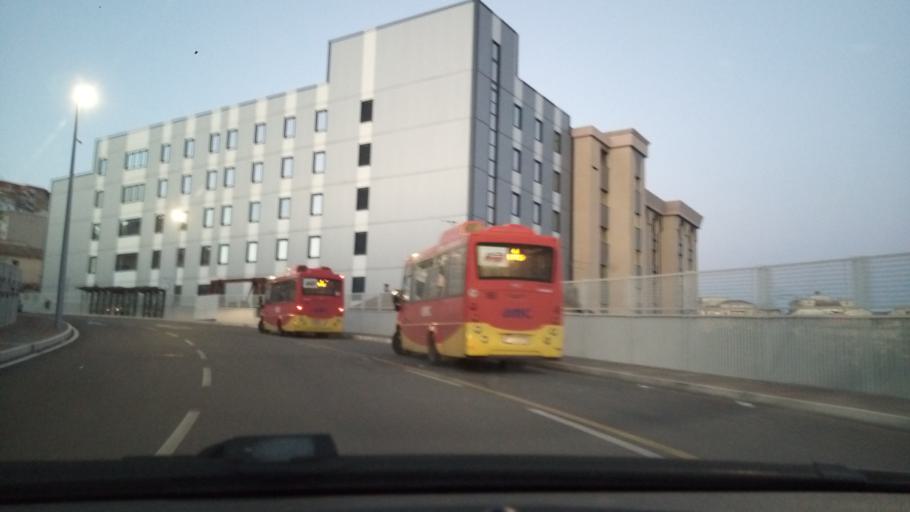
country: IT
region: Calabria
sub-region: Provincia di Catanzaro
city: Siano
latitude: 38.9111
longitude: 16.5885
